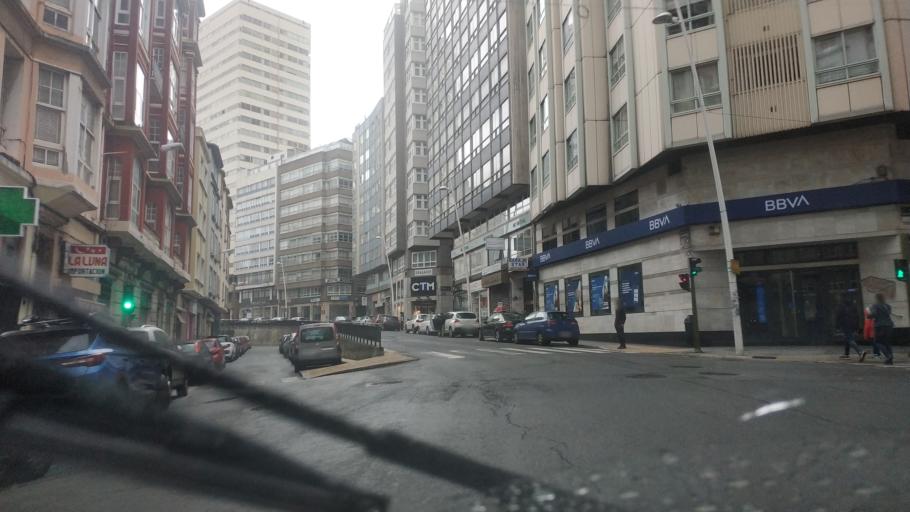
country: ES
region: Galicia
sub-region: Provincia da Coruna
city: A Coruna
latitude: 43.3621
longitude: -8.4080
